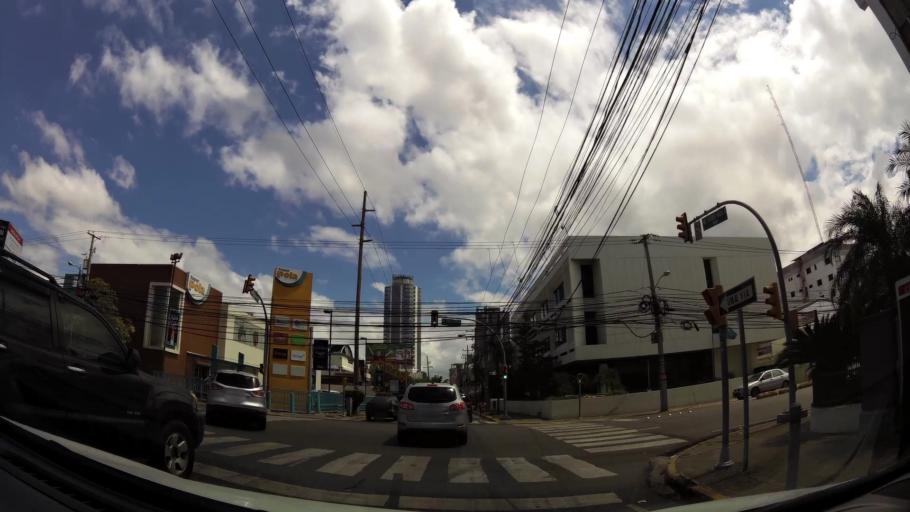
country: DO
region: Nacional
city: La Julia
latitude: 18.4755
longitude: -69.9315
